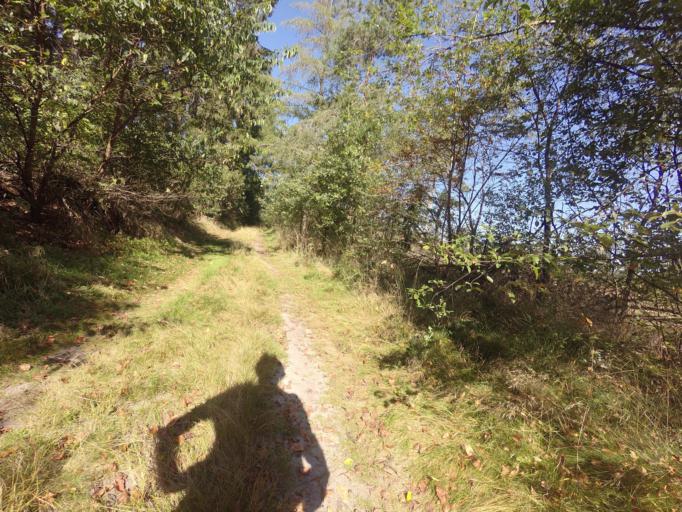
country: DE
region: Lower Saxony
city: Wielen
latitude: 52.5357
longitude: 6.7016
